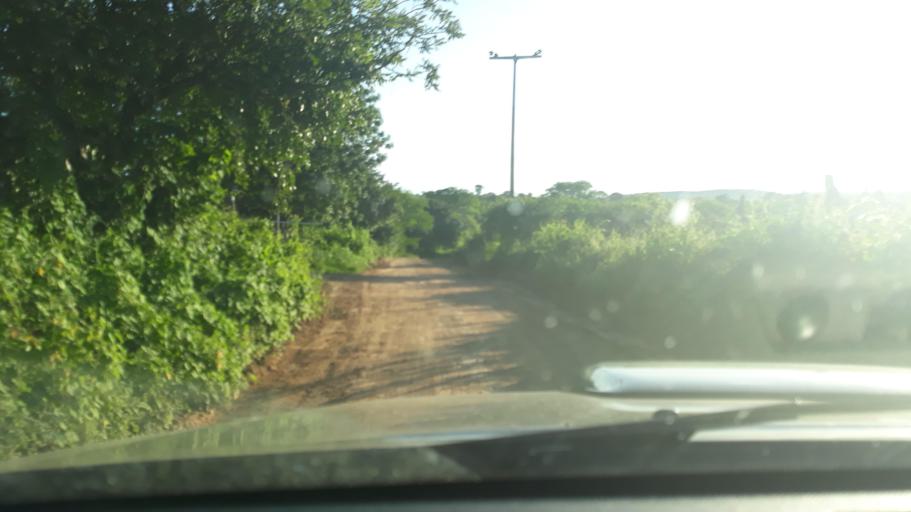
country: BR
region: Bahia
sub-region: Riacho De Santana
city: Riacho de Santana
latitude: -13.8378
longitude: -42.7329
